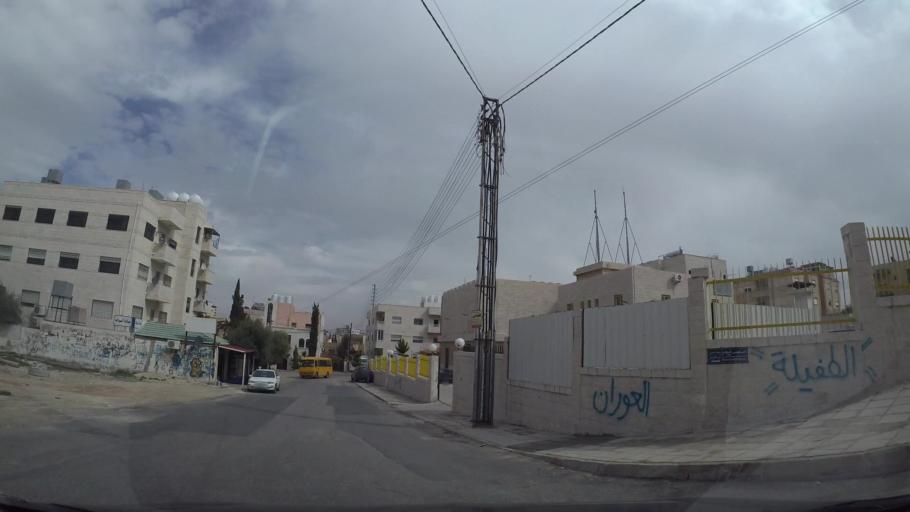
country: JO
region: Amman
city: Amman
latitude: 31.9939
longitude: 35.9426
